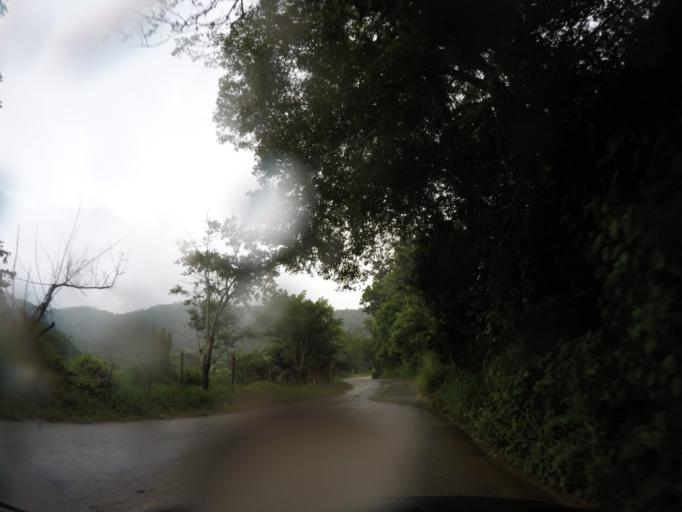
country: MX
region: Oaxaca
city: San Gabriel Mixtepec
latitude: 16.1069
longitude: -97.0642
